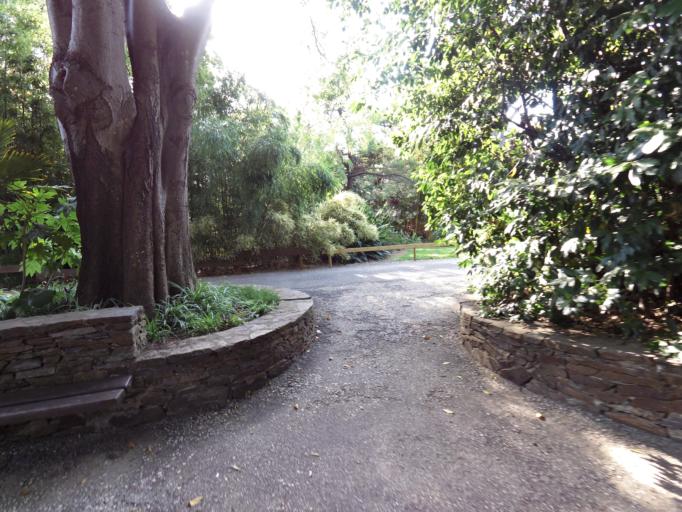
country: FR
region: Provence-Alpes-Cote d'Azur
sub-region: Departement du Var
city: Hyeres
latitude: 43.1110
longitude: 6.1354
